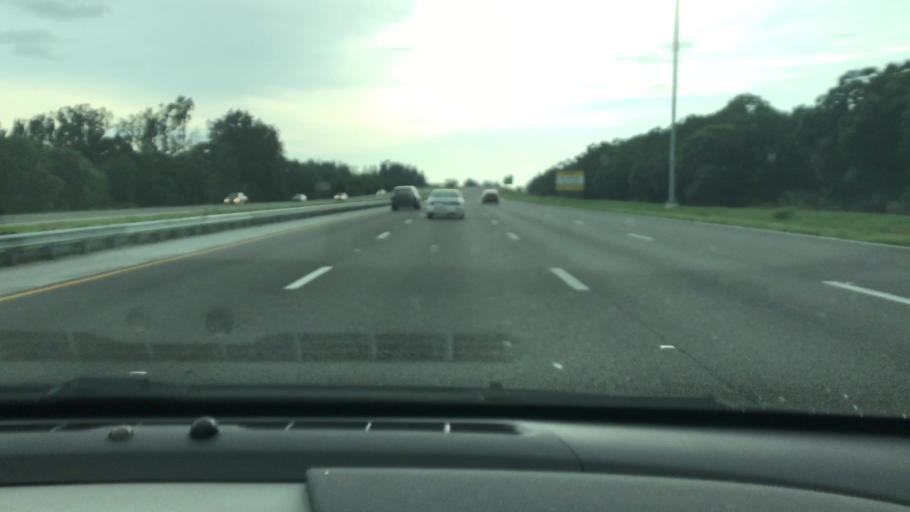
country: US
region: Florida
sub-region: Sarasota County
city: Plantation
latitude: 27.1098
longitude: -82.3538
